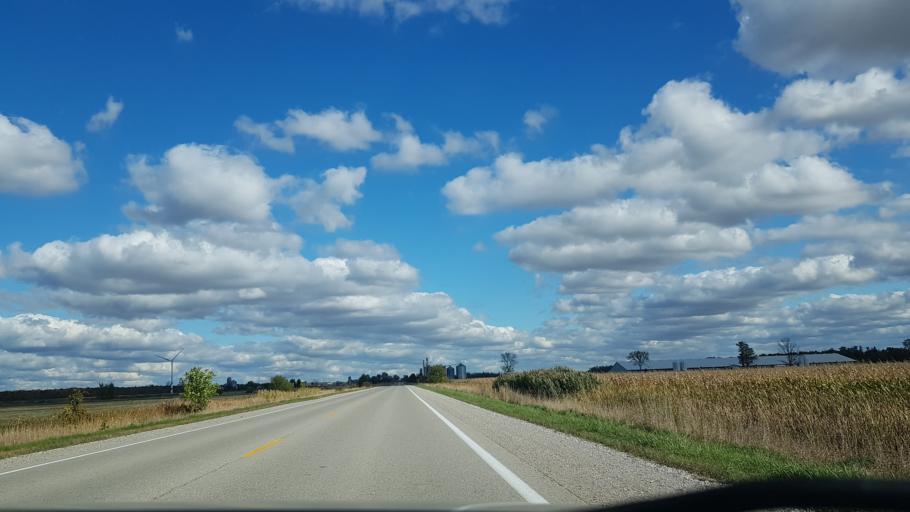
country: CA
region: Ontario
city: Lambton Shores
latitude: 43.2381
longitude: -81.7592
